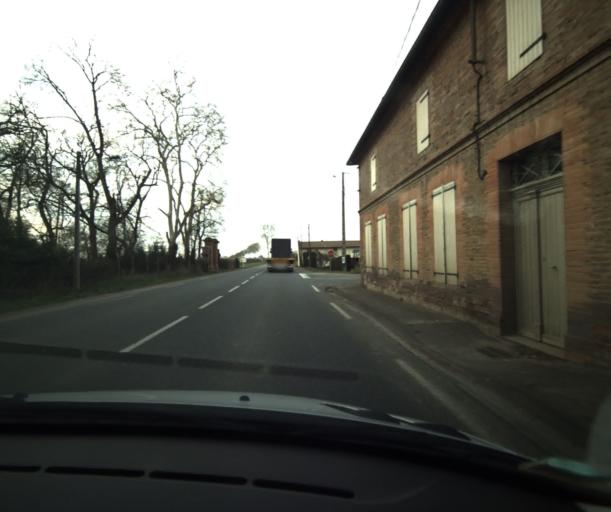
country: FR
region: Midi-Pyrenees
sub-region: Departement du Tarn-et-Garonne
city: Saint-Porquier
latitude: 44.0207
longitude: 1.1569
